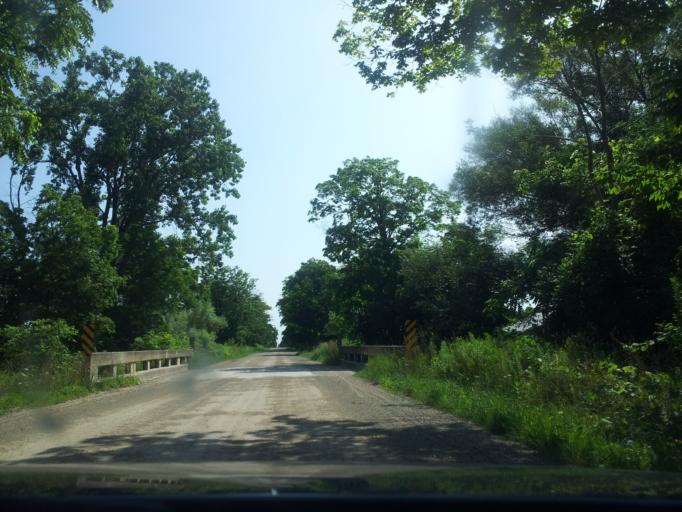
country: CA
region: Ontario
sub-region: Oxford County
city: Woodstock
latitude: 42.9533
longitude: -80.6247
